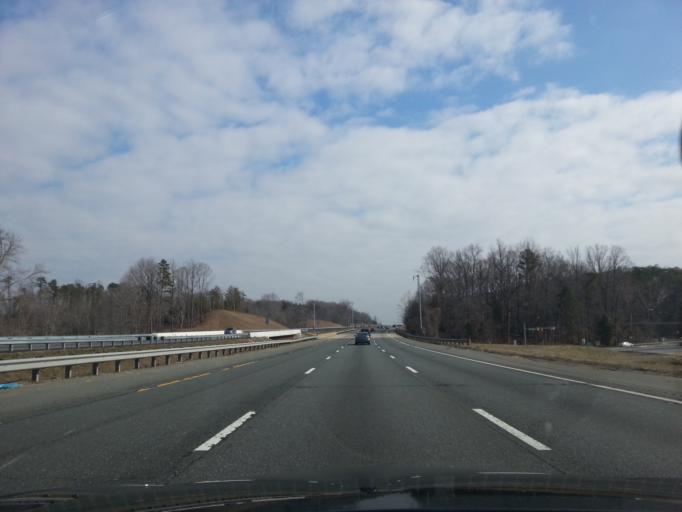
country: US
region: Virginia
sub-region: Prince William County
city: Triangle
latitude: 38.5212
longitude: -77.3702
